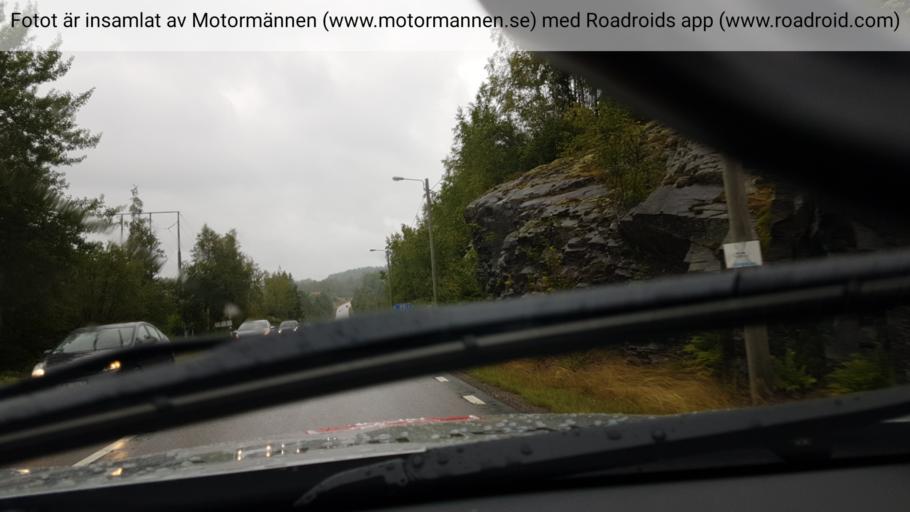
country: SE
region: Vaestra Goetaland
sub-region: Bengtsfors Kommun
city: Bengtsfors
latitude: 59.0224
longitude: 12.2769
